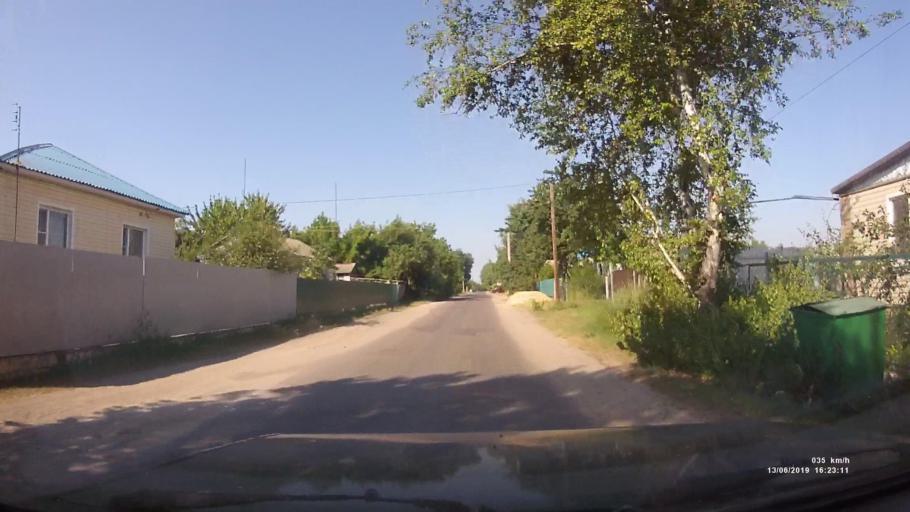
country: RU
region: Rostov
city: Kazanskaya
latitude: 49.7926
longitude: 41.1370
